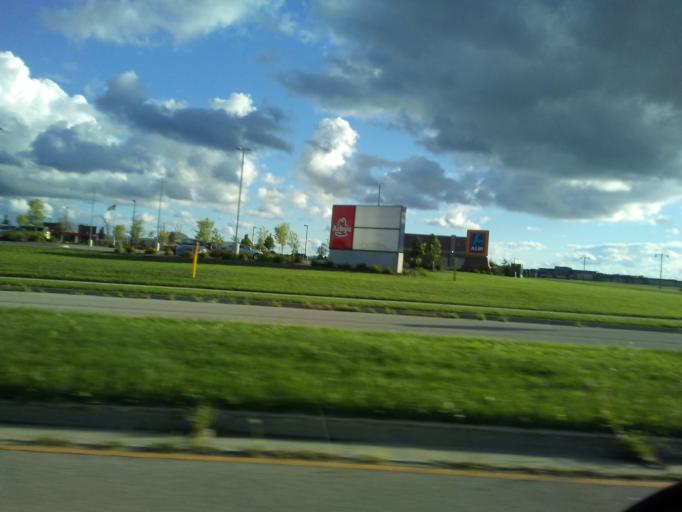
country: US
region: Wisconsin
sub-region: Dane County
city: Sun Prairie
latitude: 43.1688
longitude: -89.2662
